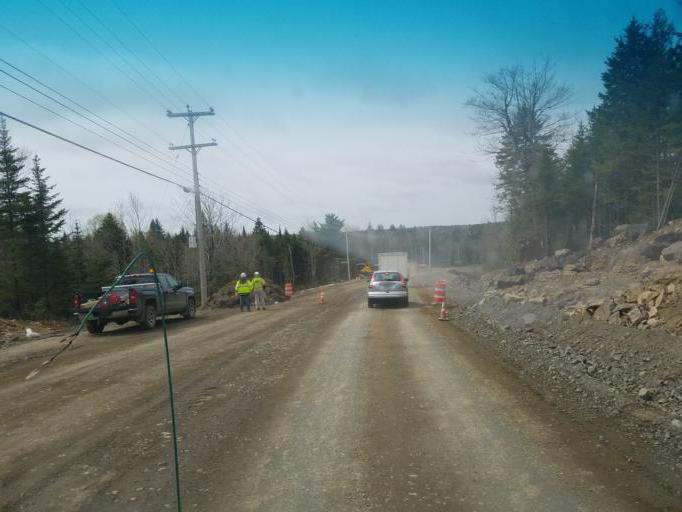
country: US
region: Maine
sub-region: Washington County
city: East Machias
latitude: 44.7686
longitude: -67.1979
